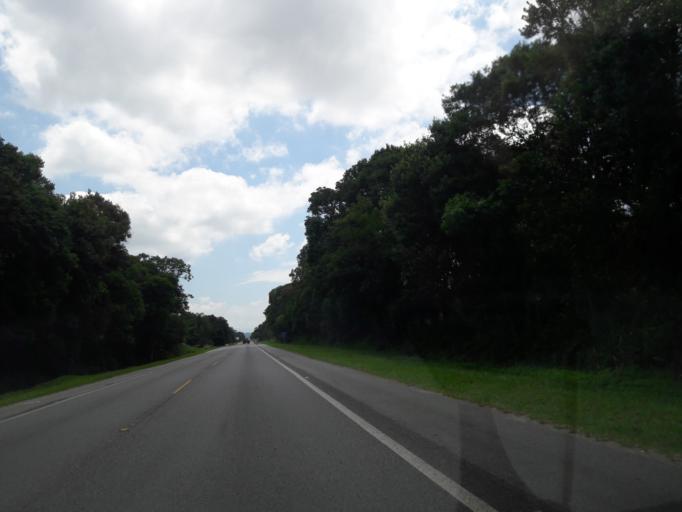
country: BR
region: Parana
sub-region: Pontal Do Parana
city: Pontal do Parana
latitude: -25.6010
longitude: -48.5578
